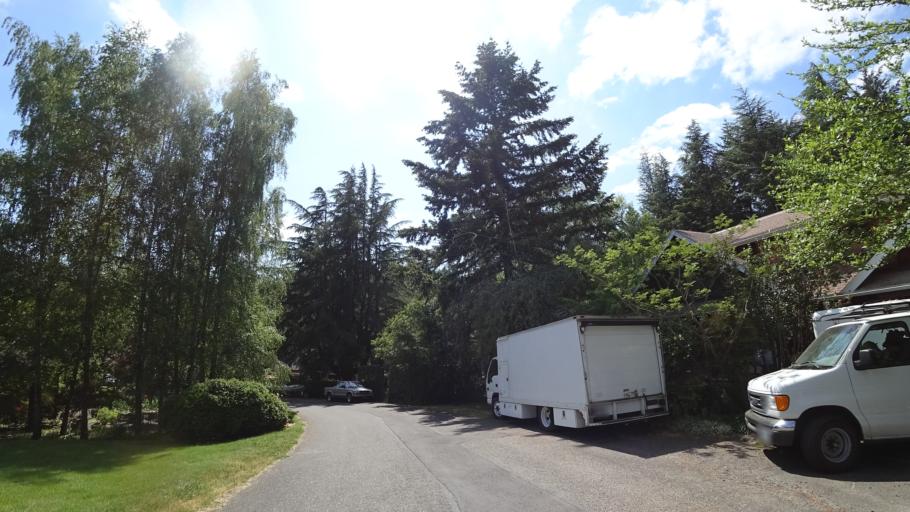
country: US
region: Oregon
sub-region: Washington County
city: Raleigh Hills
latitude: 45.4830
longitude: -122.7101
